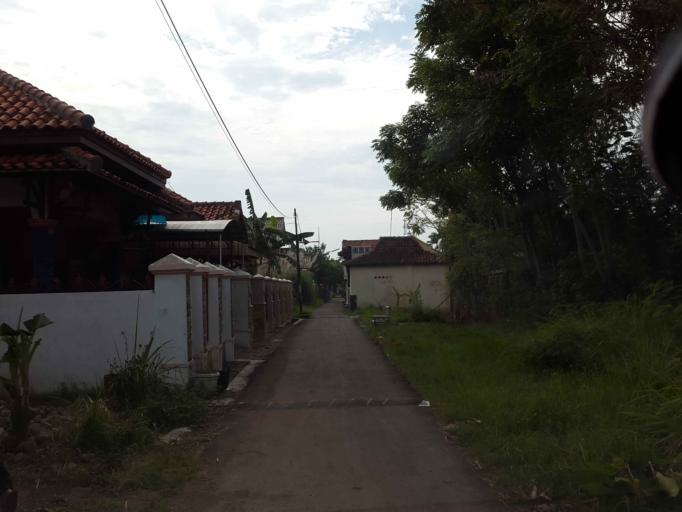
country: ID
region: Central Java
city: Dukuhturi
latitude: -6.8722
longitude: 109.0535
